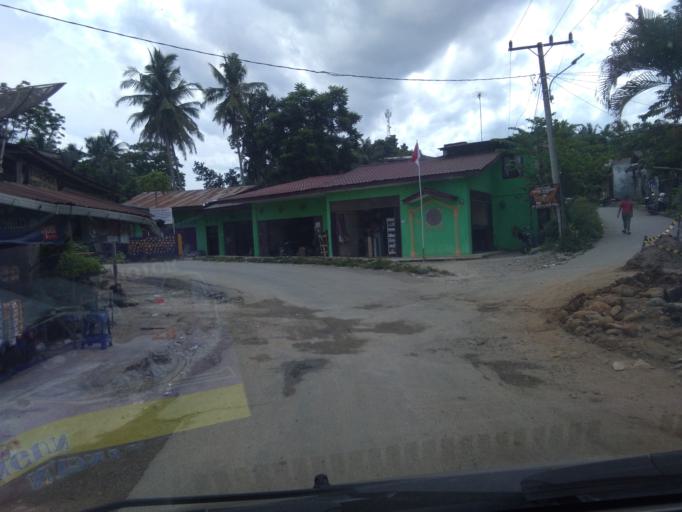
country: ID
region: North Sumatra
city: Deli Tua
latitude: 3.3059
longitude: 98.8091
